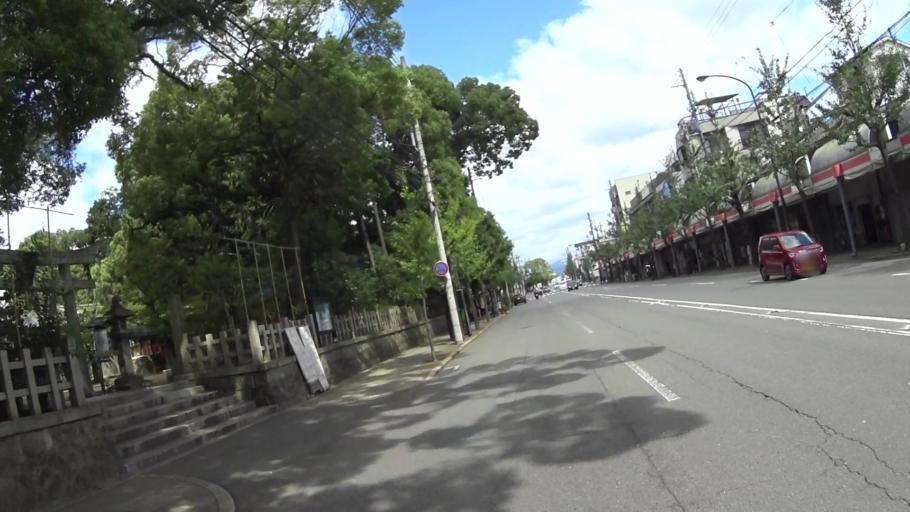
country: JP
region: Kyoto
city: Kyoto
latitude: 34.9843
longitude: 135.7739
